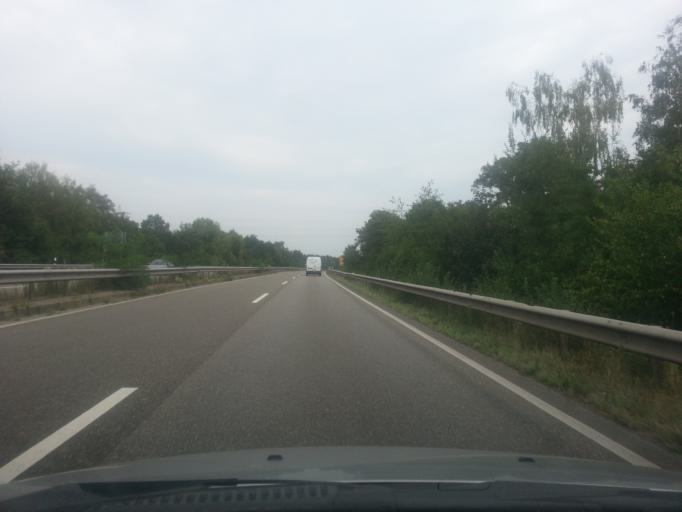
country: DE
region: Rheinland-Pfalz
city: Speyer
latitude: 49.3383
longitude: 8.4108
